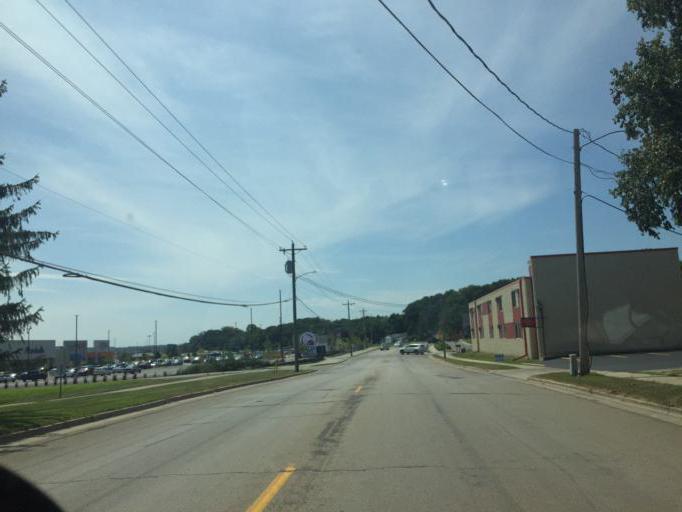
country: US
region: Minnesota
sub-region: Olmsted County
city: Rochester
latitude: 43.9902
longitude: -92.4606
